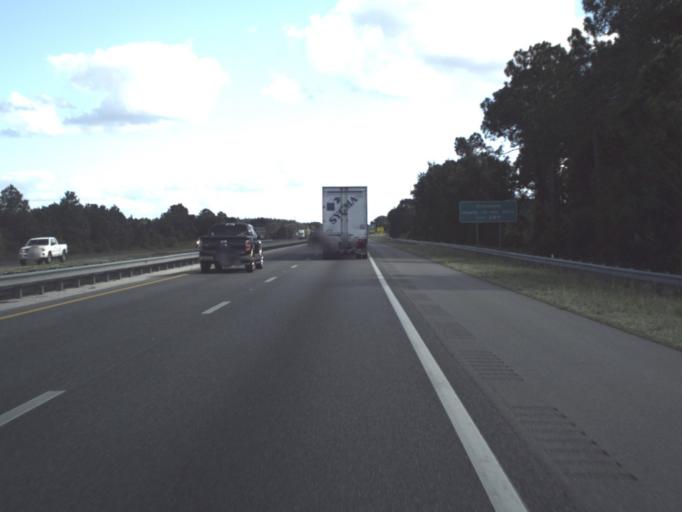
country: US
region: Florida
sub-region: Lake County
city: Hawthorne
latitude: 28.6901
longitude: -81.8702
